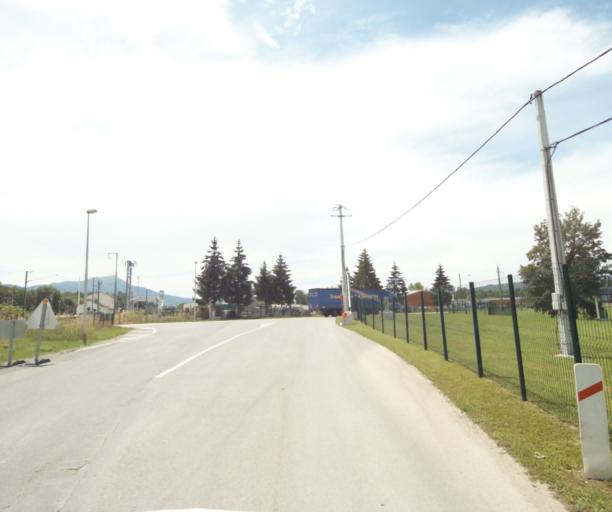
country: FR
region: Rhone-Alpes
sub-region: Departement de la Haute-Savoie
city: Perrignier
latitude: 46.3044
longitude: 6.4260
